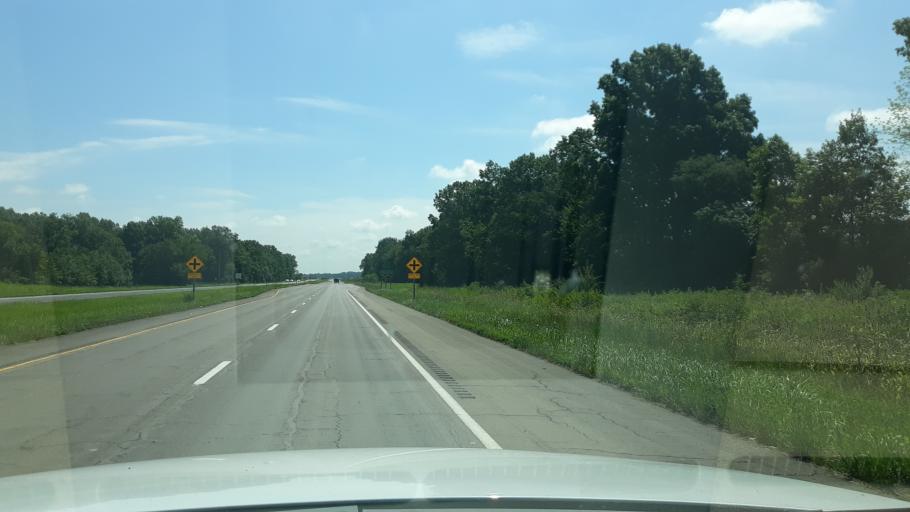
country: US
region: Illinois
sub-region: Saline County
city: Carrier Mills
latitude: 37.7334
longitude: -88.6376
